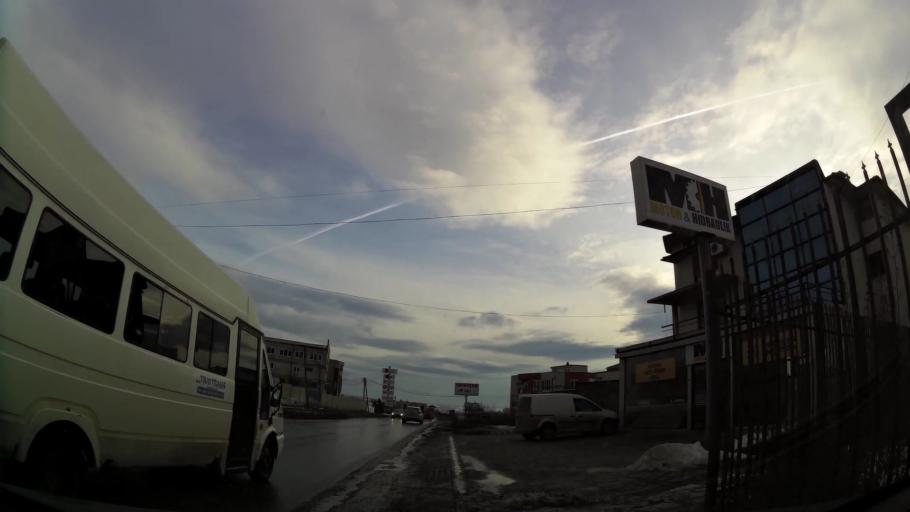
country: XK
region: Pristina
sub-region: Komuna e Prishtines
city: Pristina
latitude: 42.6263
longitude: 21.1611
